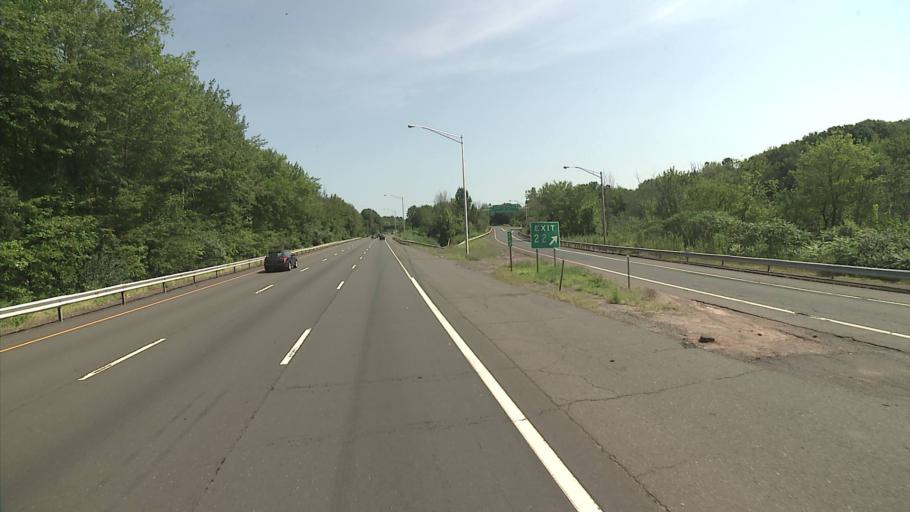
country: US
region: Connecticut
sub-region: Middlesex County
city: Cromwell
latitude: 41.6182
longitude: -72.6951
